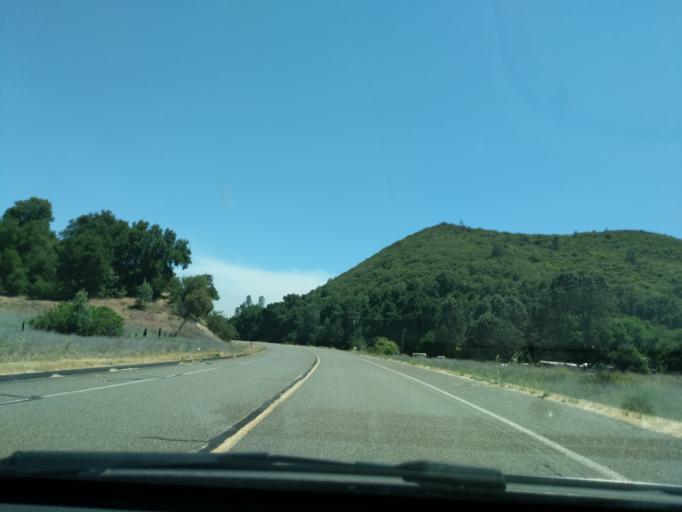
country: US
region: California
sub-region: Monterey County
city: King City
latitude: 36.0619
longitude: -121.1849
